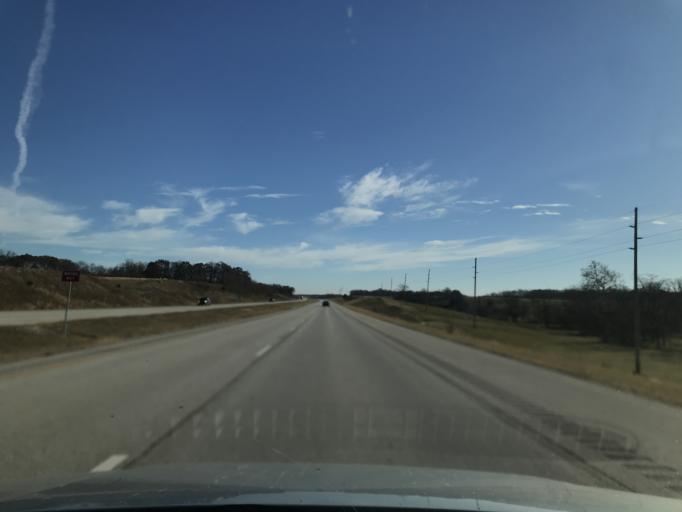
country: US
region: Illinois
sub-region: Hancock County
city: Carthage
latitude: 40.4145
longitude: -91.0336
